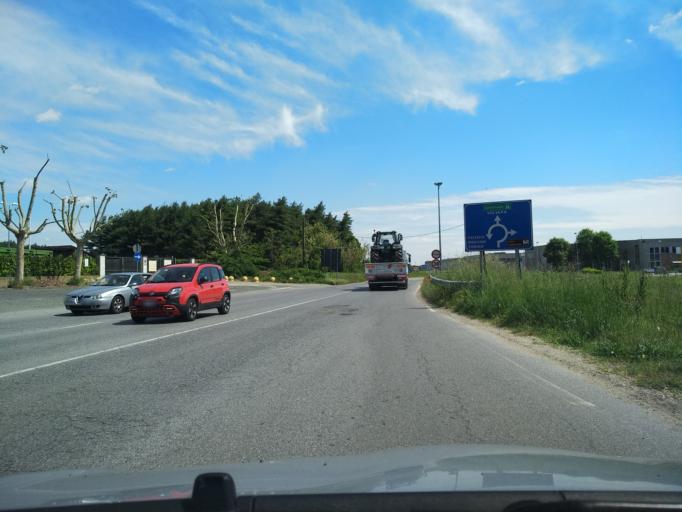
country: IT
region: Piedmont
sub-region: Provincia di Torino
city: Piossasco
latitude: 44.9774
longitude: 7.4755
